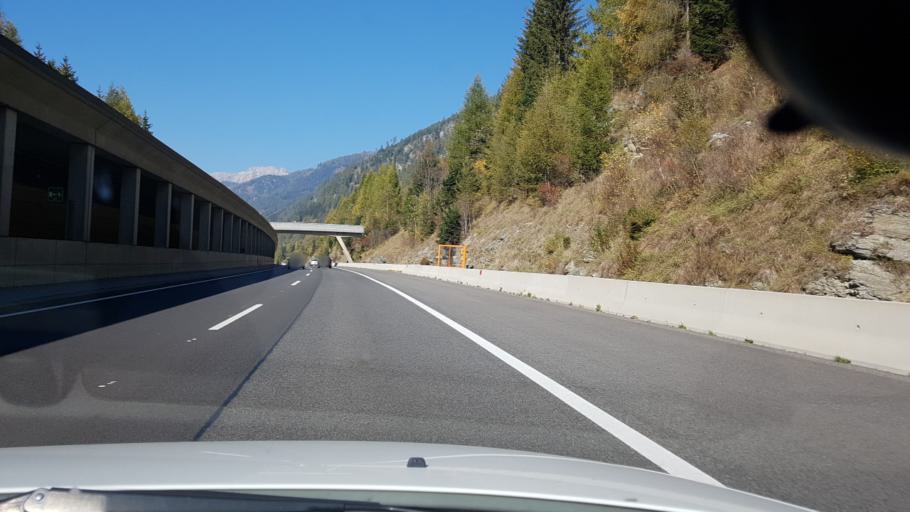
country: AT
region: Salzburg
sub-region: Politischer Bezirk Tamsweg
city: Sankt Michael im Lungau
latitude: 47.1050
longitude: 13.5970
